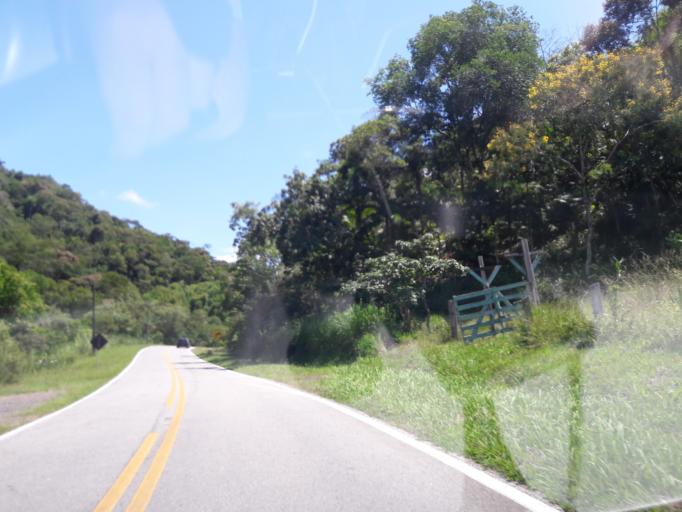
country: BR
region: Parana
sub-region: Antonina
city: Antonina
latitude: -25.5245
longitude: -48.7625
